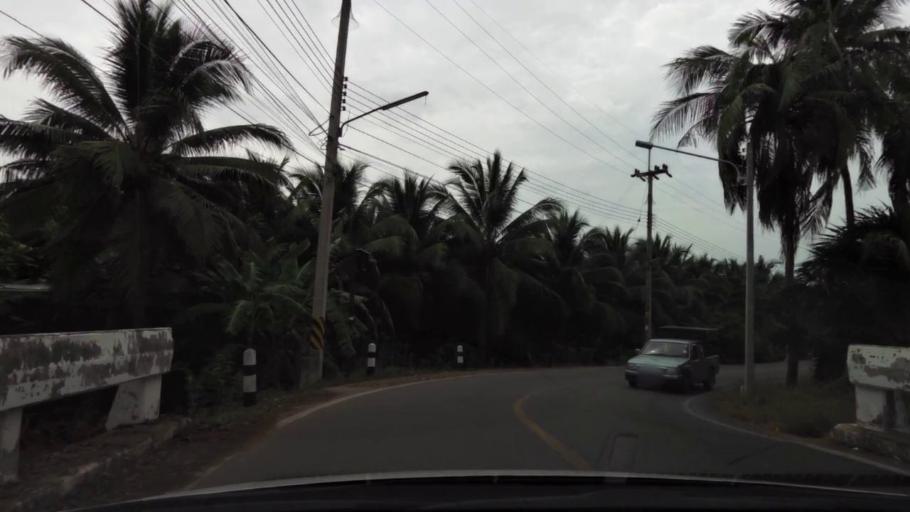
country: TH
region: Ratchaburi
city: Damnoen Saduak
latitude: 13.5692
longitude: 100.0072
